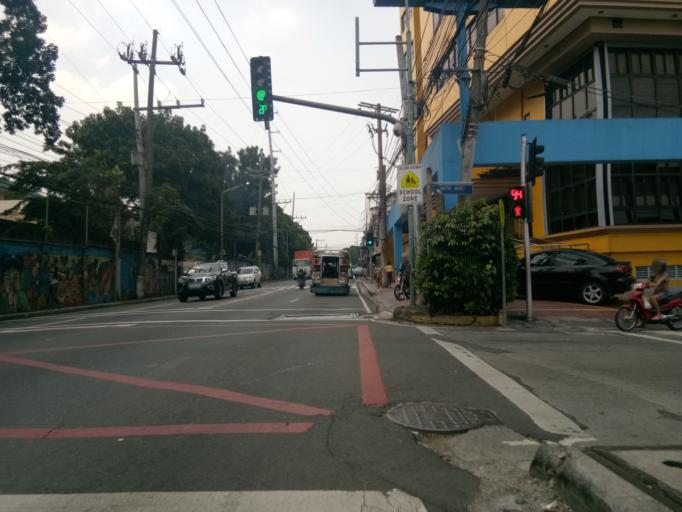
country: PH
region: Metro Manila
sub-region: Pasig
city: Pasig City
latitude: 14.6133
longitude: 121.0647
